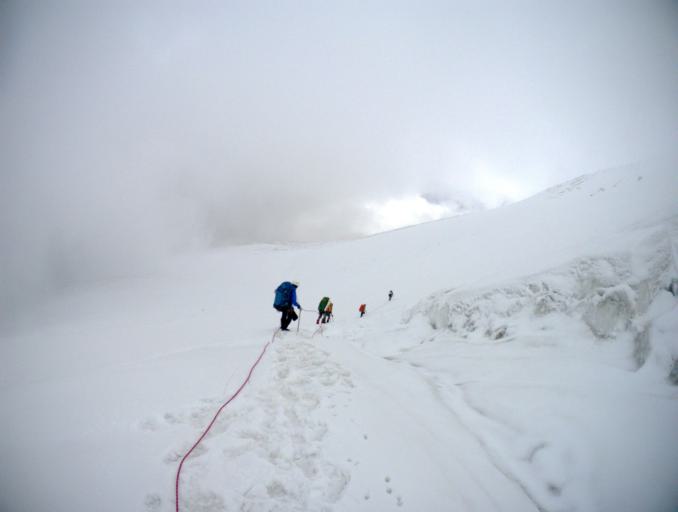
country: RU
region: Kabardino-Balkariya
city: Terskol
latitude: 43.3702
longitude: 42.4849
